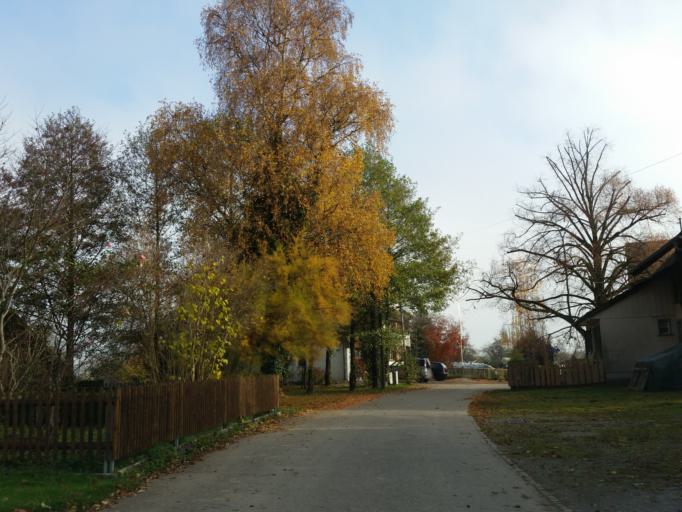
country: CH
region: Thurgau
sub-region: Arbon District
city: Arbon
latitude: 47.5308
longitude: 9.4077
